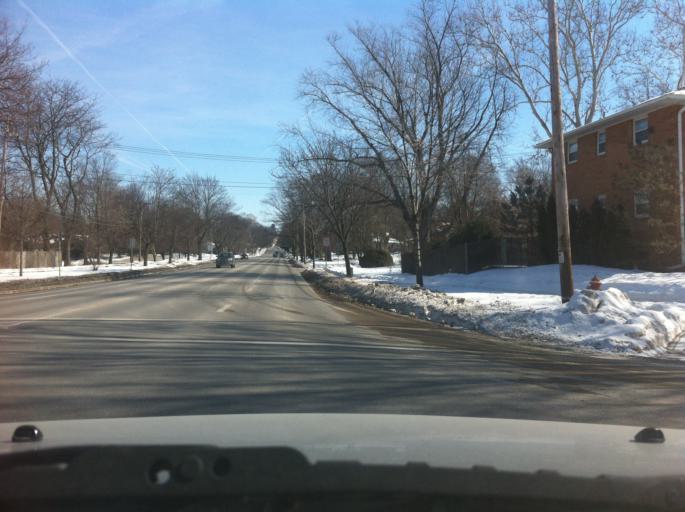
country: US
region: Wisconsin
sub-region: Dane County
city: Shorewood Hills
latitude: 43.0609
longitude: -89.4628
